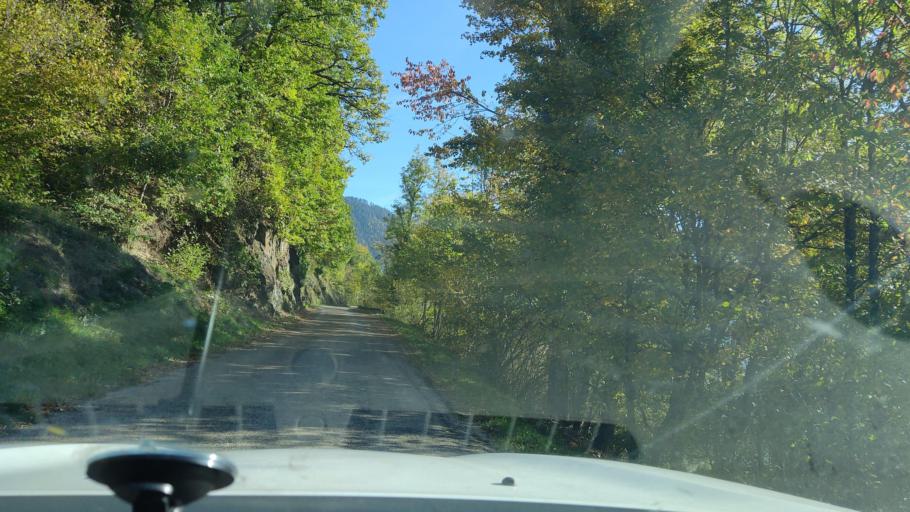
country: FR
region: Rhone-Alpes
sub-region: Departement de la Savoie
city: Beaufort
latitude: 45.7245
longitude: 6.5097
